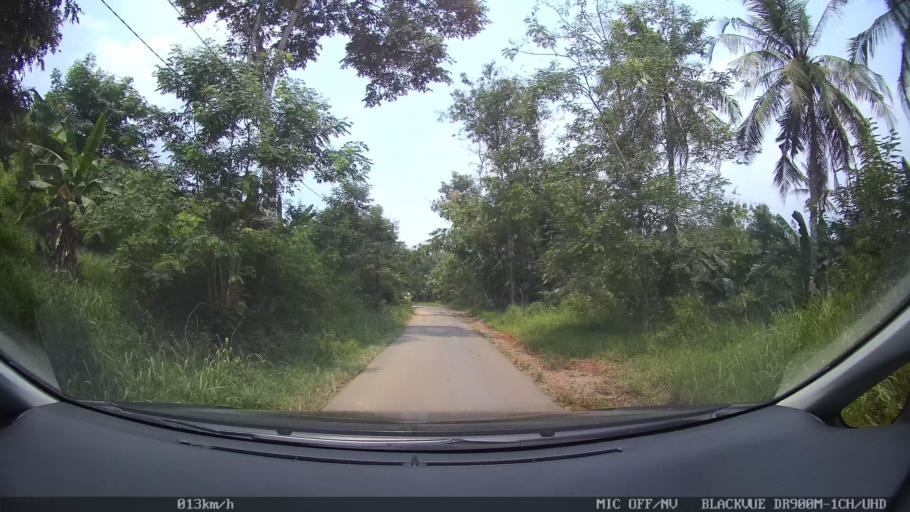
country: ID
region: Lampung
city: Pringsewu
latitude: -5.3829
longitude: 105.0093
